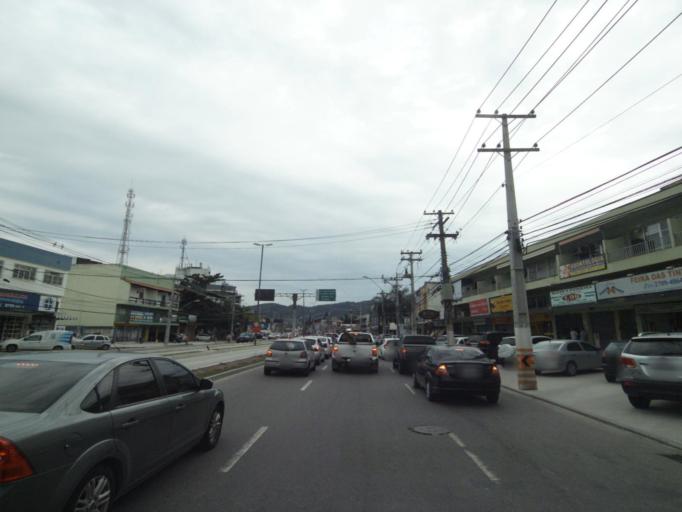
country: BR
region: Rio de Janeiro
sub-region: Niteroi
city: Niteroi
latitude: -22.9461
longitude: -43.0324
